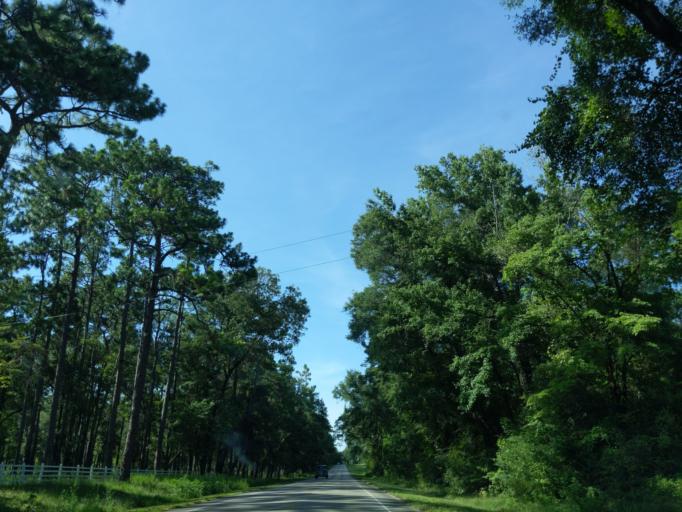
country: US
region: Florida
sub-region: Leon County
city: Woodville
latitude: 30.2766
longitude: -84.3125
